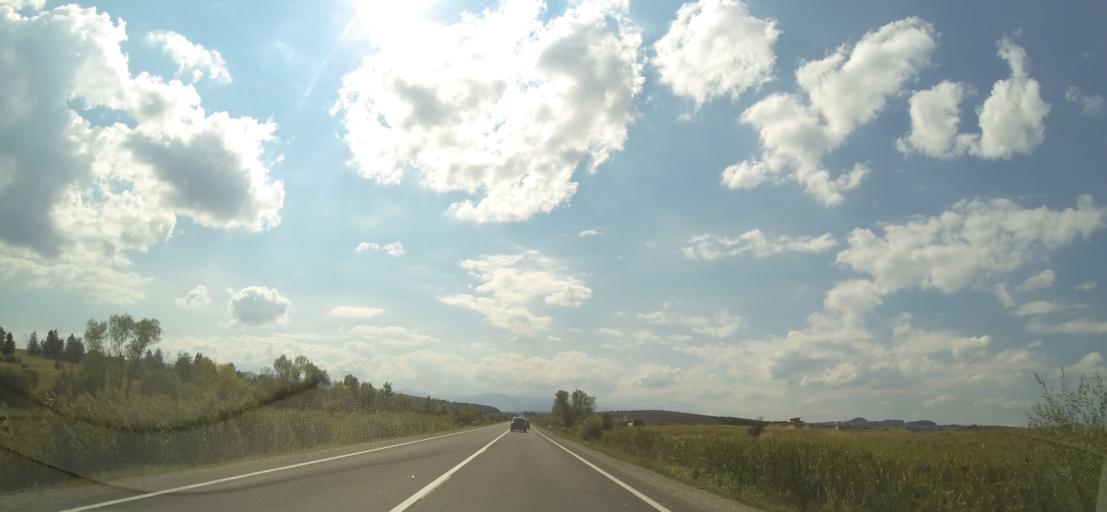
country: RO
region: Brasov
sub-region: Comuna Dumbravita
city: Dumbravita
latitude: 45.7716
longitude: 25.3379
